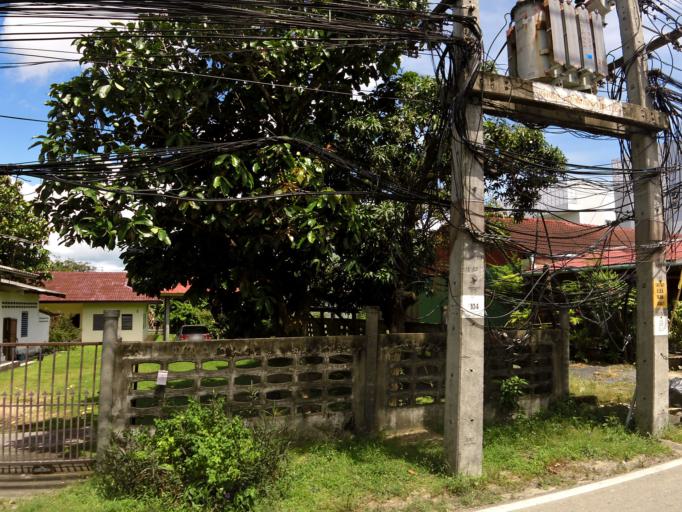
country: TH
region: Phuket
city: Ban Chalong
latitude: 7.8438
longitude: 98.3345
